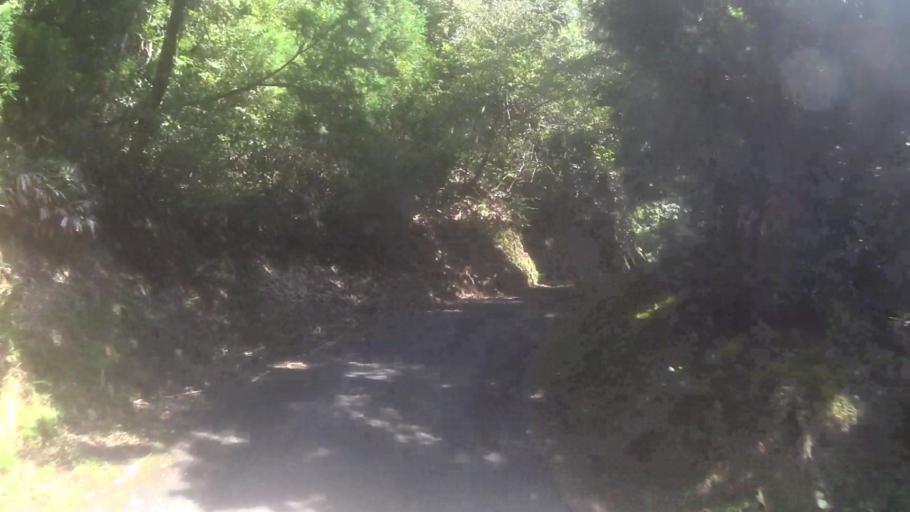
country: JP
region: Kyoto
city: Miyazu
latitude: 35.6633
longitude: 135.1279
